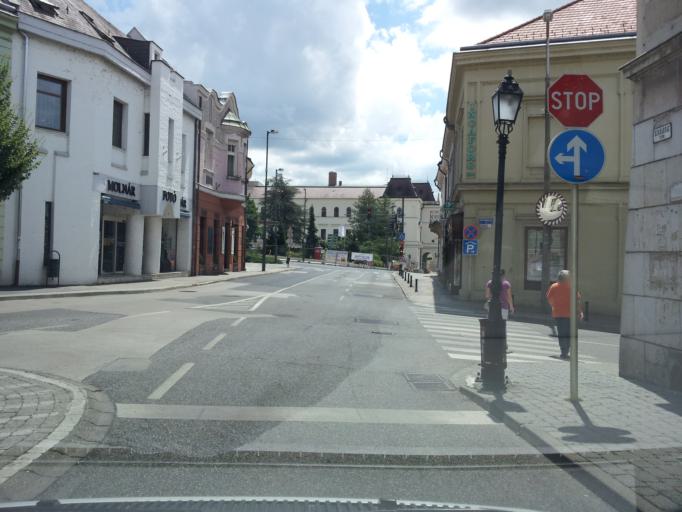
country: HU
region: Veszprem
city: Veszprem
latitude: 47.0932
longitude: 17.9075
